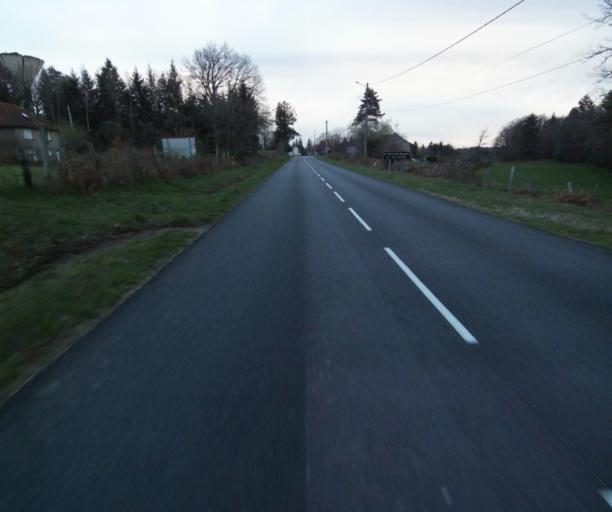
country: FR
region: Limousin
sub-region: Departement de la Correze
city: Correze
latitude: 45.3441
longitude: 1.8747
